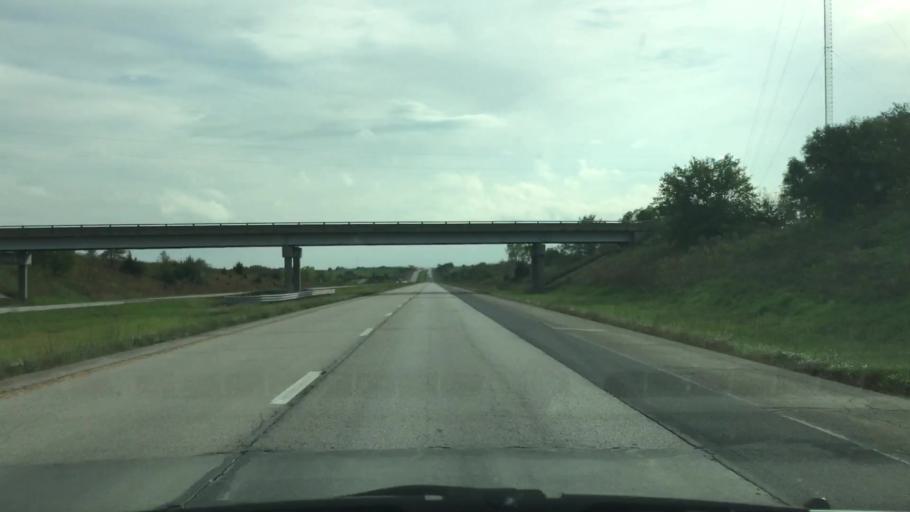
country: US
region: Iowa
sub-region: Decatur County
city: Lamoni
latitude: 40.5158
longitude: -93.9632
